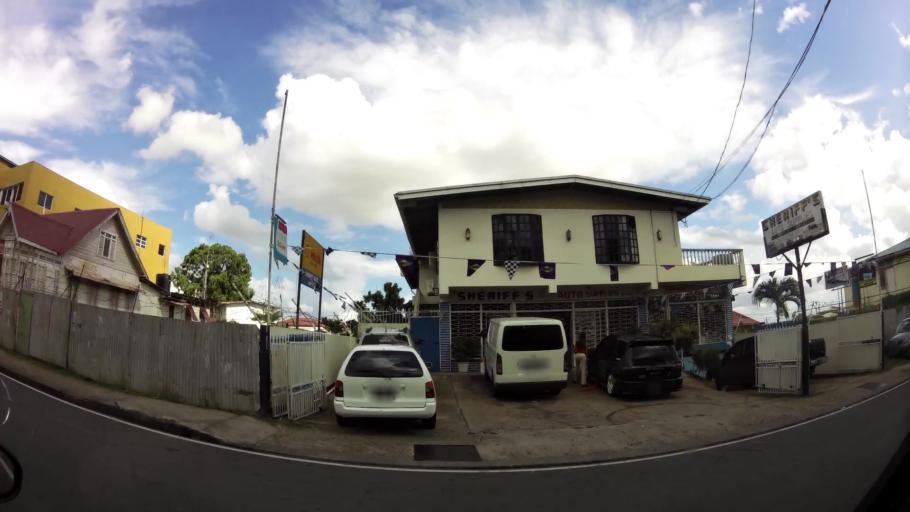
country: TT
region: City of San Fernando
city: San Fernando
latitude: 10.2764
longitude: -61.4602
